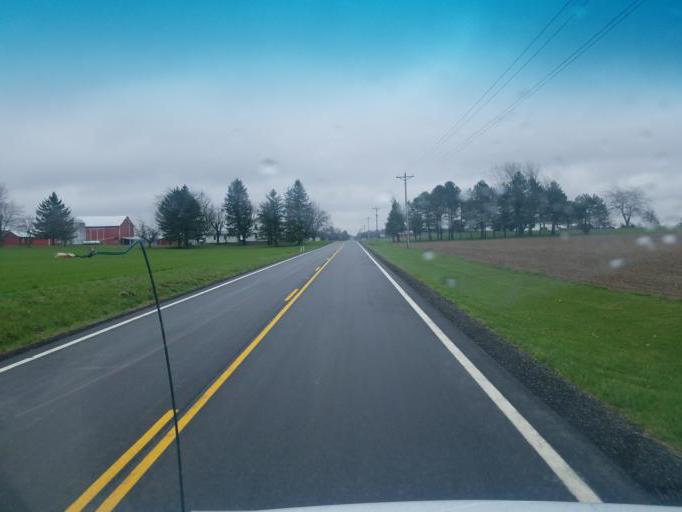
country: US
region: Ohio
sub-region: Huron County
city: Willard
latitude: 40.9603
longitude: -82.8216
